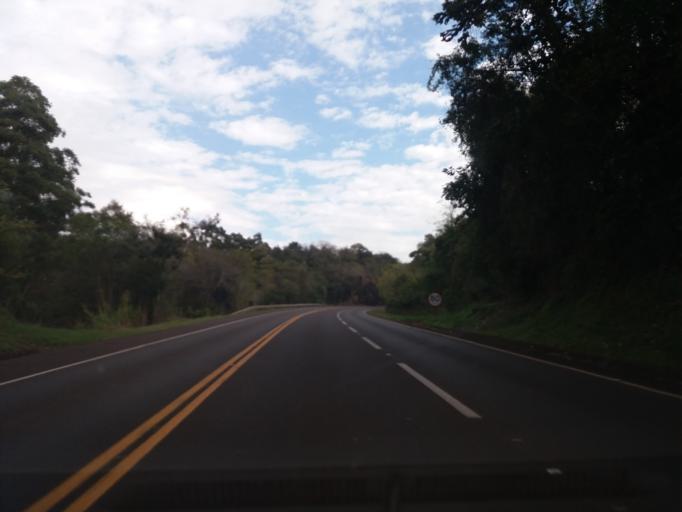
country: BR
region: Parana
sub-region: Corbelia
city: Corbelia
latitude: -24.5773
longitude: -53.1479
